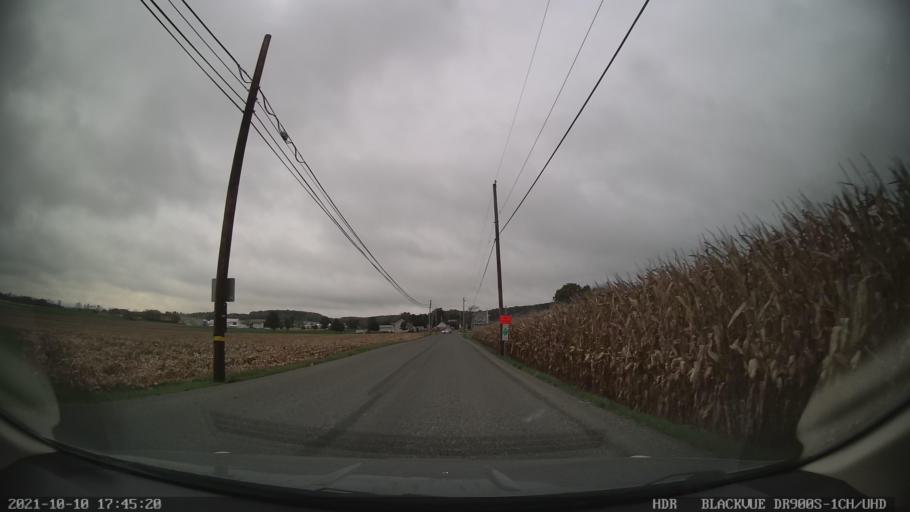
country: US
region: Pennsylvania
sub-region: Lehigh County
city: Breinigsville
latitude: 40.5512
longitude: -75.6761
